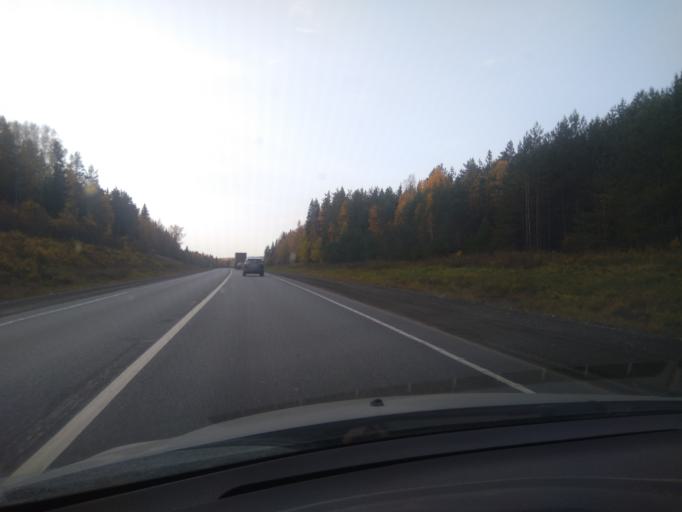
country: RU
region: Sverdlovsk
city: Druzhinino
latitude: 56.8174
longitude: 59.5636
